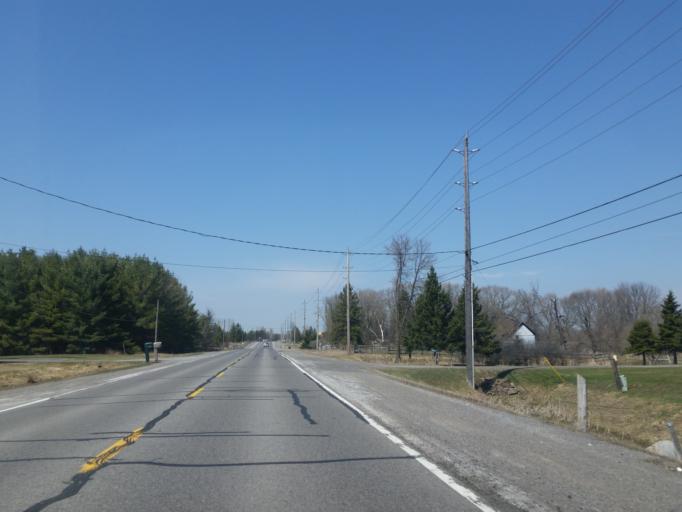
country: CA
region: Ontario
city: Bells Corners
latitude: 45.4455
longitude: -76.0527
